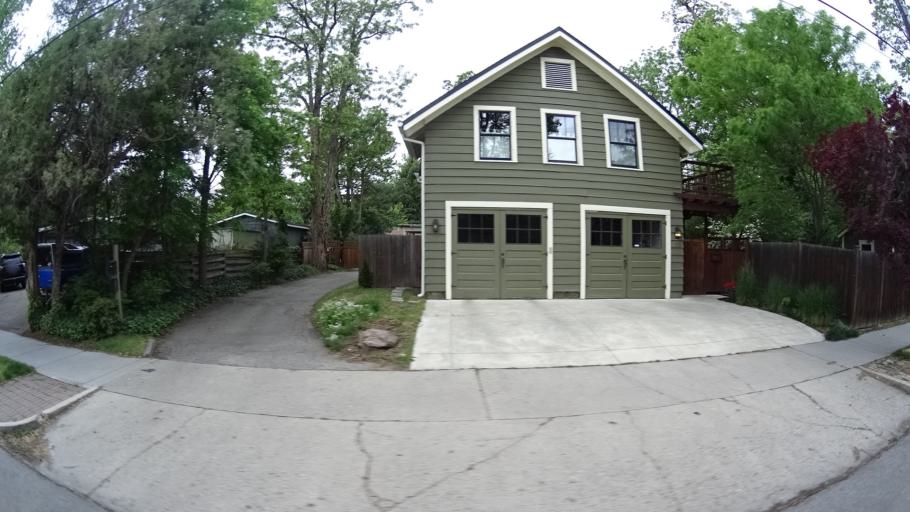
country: US
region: Idaho
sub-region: Ada County
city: Boise
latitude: 43.6064
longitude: -116.1832
